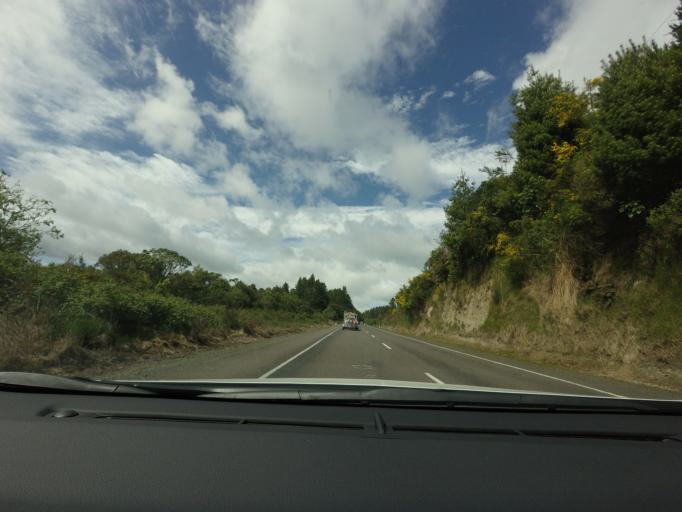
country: NZ
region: Bay of Plenty
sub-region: Rotorua District
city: Rotorua
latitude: -38.3226
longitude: 176.3721
